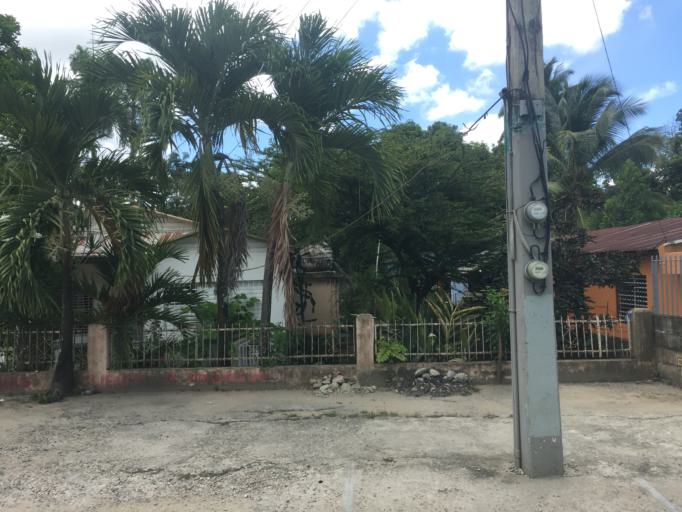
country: DO
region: Santiago
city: Tamboril
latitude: 19.4855
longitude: -70.6592
